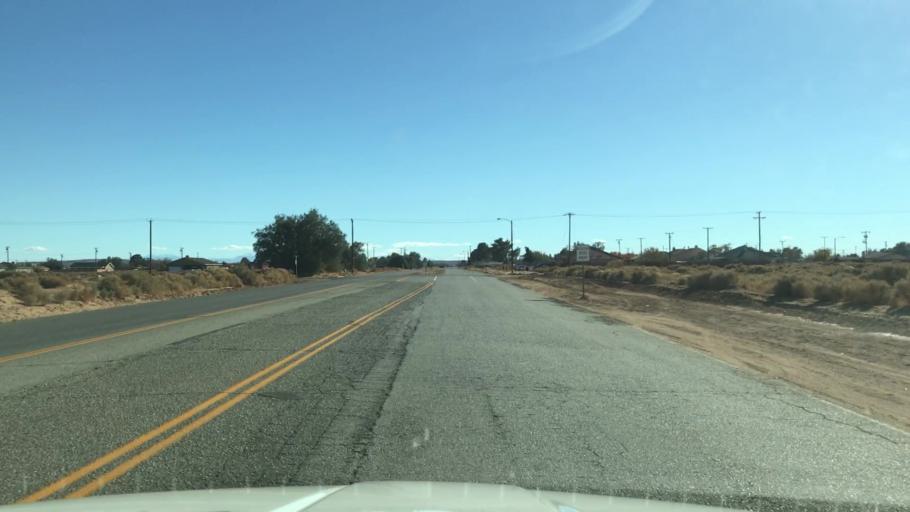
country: US
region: California
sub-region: Kern County
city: California City
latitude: 35.1342
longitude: -117.9858
